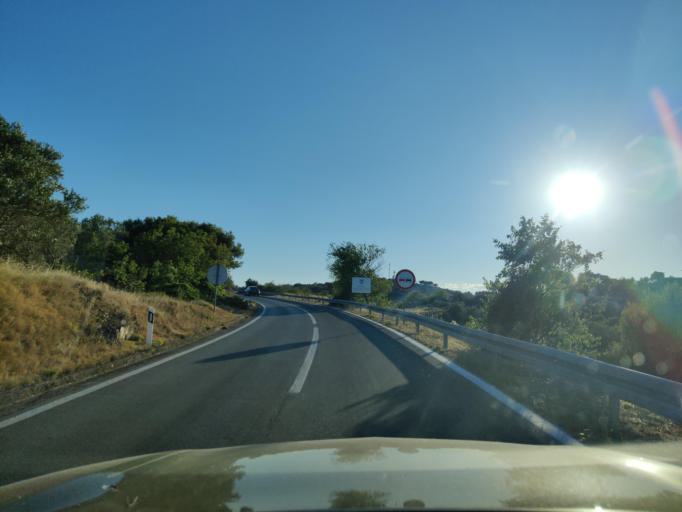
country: HR
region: Sibensko-Kniniska
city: Murter
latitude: 43.8122
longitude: 15.5981
